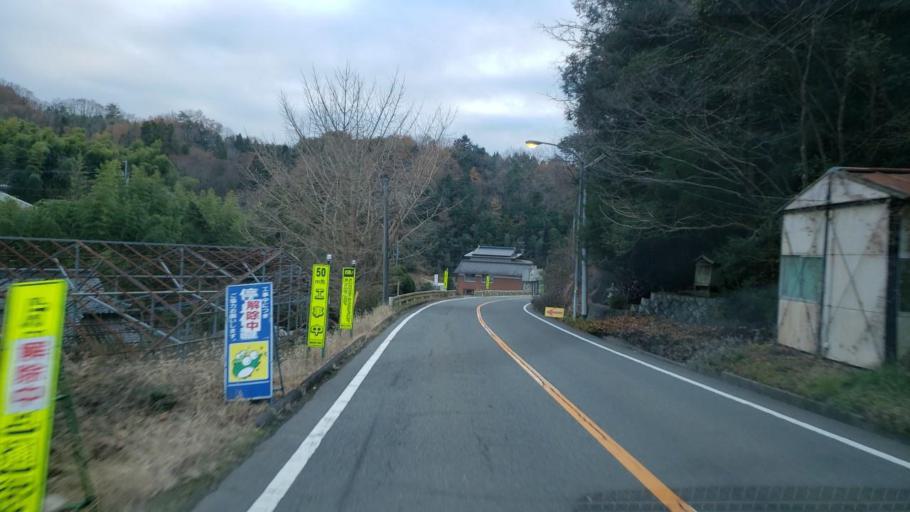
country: JP
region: Tokushima
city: Wakimachi
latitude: 34.1908
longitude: 134.1748
